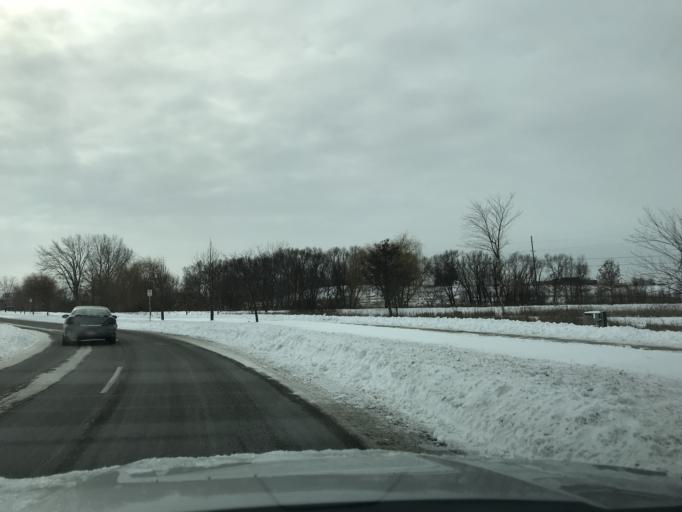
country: US
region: Wisconsin
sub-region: Dane County
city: Sun Prairie
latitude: 43.1613
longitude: -89.2638
